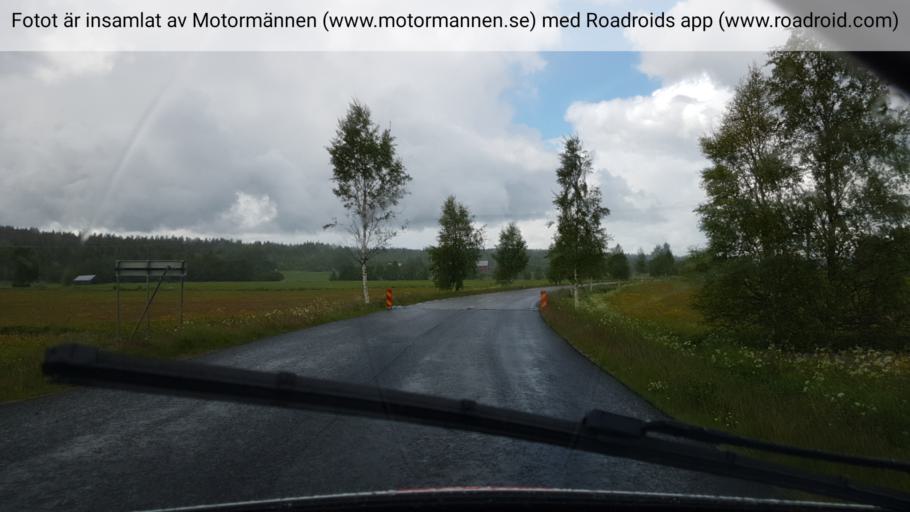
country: SE
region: Vaesterbotten
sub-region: Vannas Kommun
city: Vannasby
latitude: 63.8520
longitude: 19.9082
